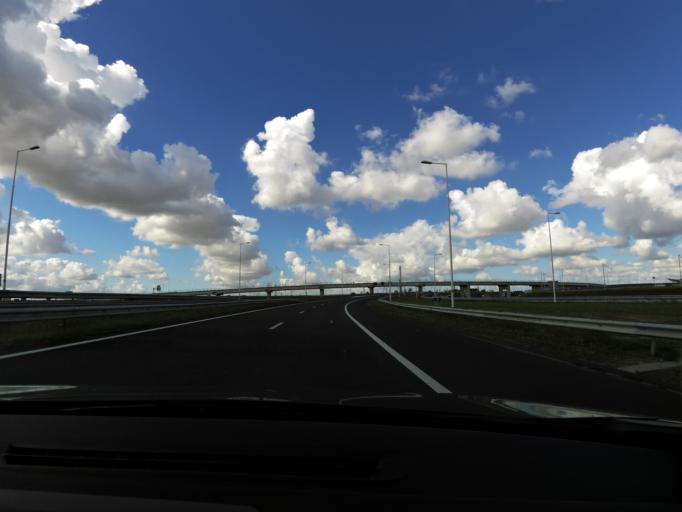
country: NL
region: South Holland
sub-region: Gemeente Albrandswaard
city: Rhoon
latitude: 51.8744
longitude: 4.3918
